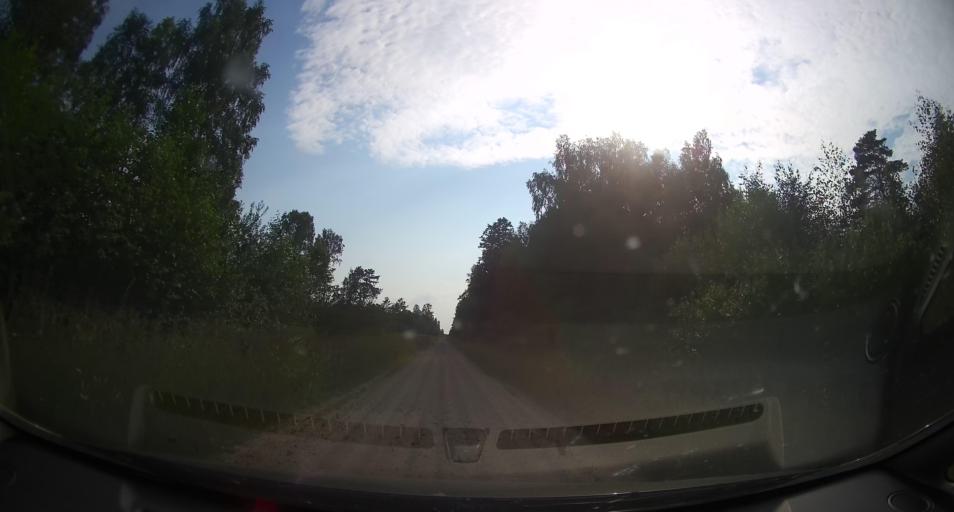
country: EE
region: Laeaene
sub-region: Lihula vald
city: Lihula
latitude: 58.6385
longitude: 23.7605
